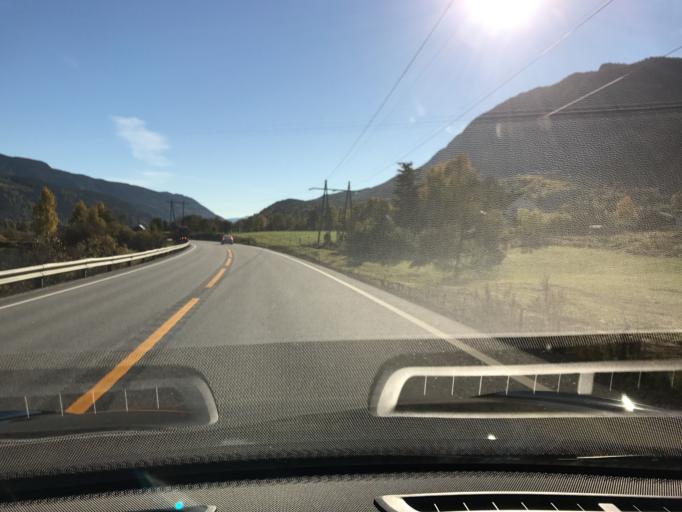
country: NO
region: Buskerud
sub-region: Nes
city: Nesbyen
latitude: 60.5646
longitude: 9.1162
